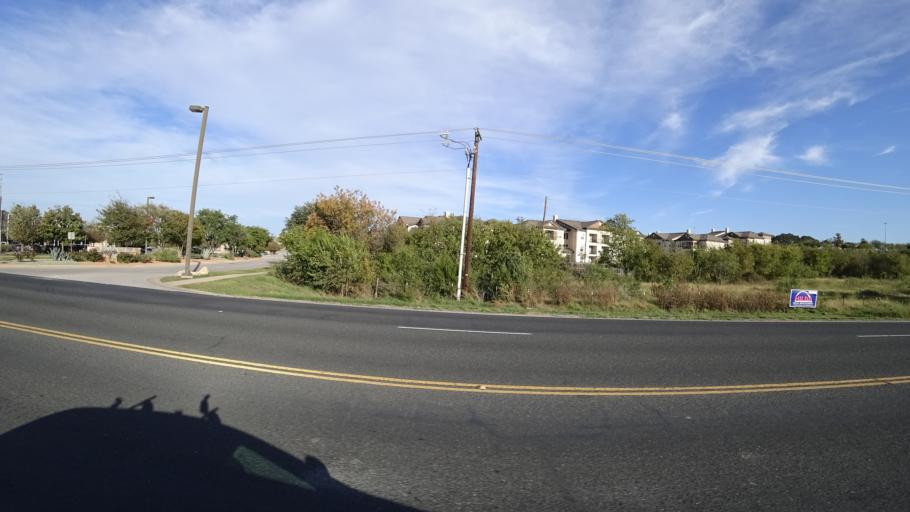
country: US
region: Texas
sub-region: Williamson County
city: Round Rock
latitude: 30.4822
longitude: -97.6942
